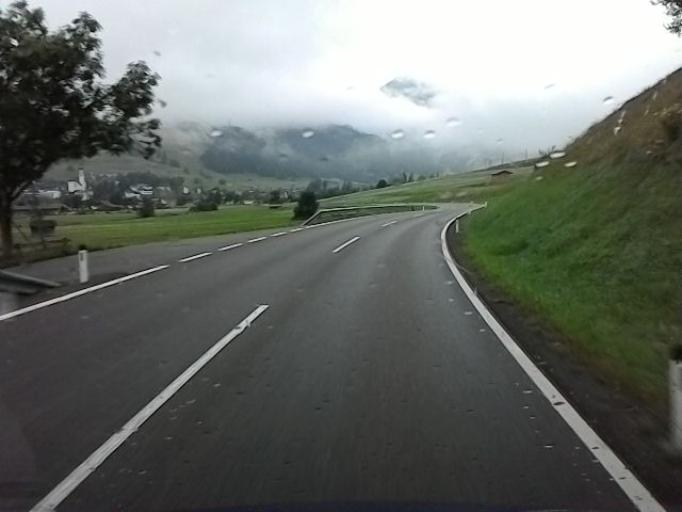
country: AT
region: Tyrol
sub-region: Politischer Bezirk Reutte
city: Lermoos
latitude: 47.4043
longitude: 10.8972
